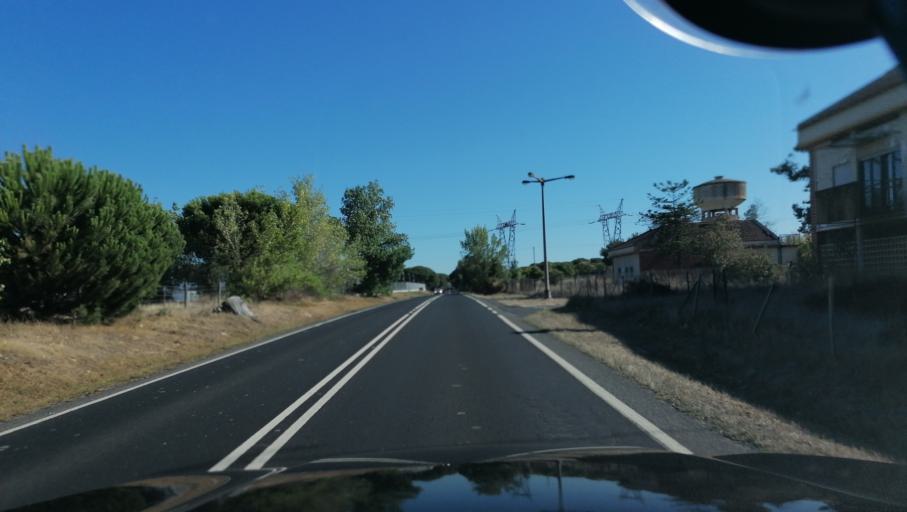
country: PT
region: Santarem
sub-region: Benavente
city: Samora Correia
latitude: 38.8996
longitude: -8.8815
